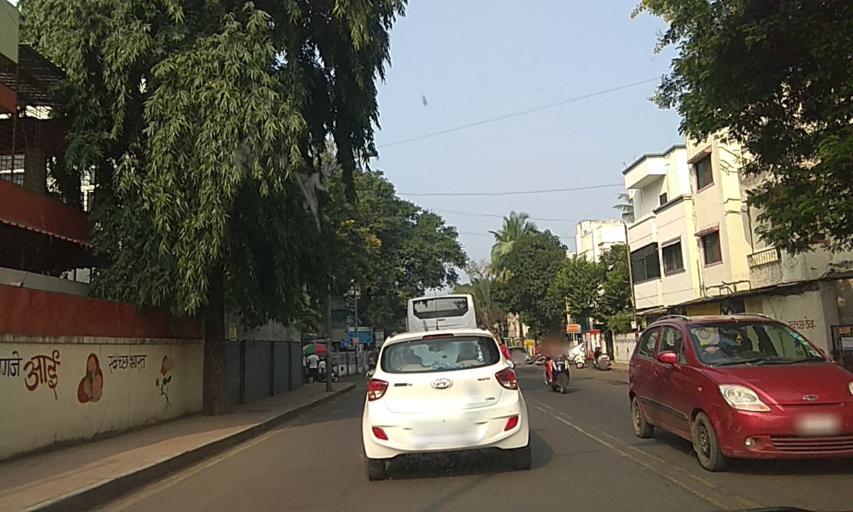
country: IN
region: Maharashtra
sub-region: Pune Division
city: Pune
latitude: 18.5054
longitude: 73.8435
